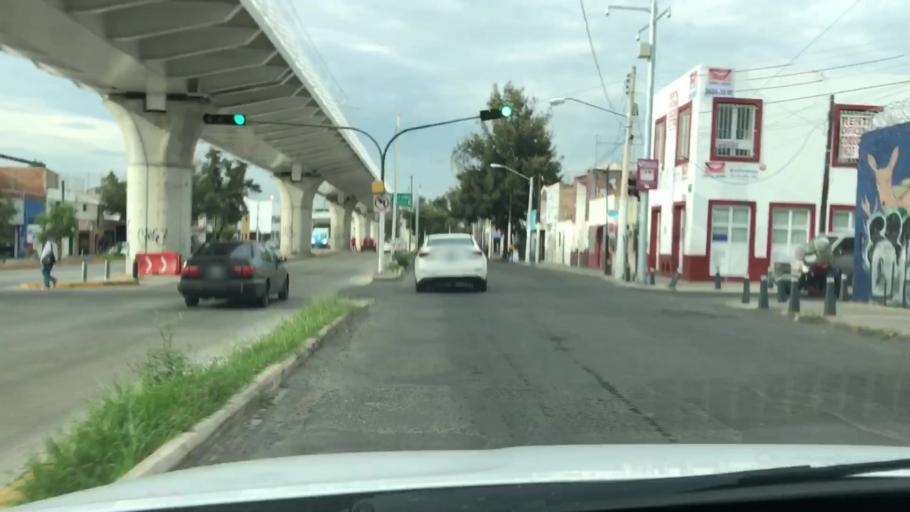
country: MX
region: Jalisco
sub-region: Zapopan
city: Zapopan
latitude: 20.7246
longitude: -103.3873
